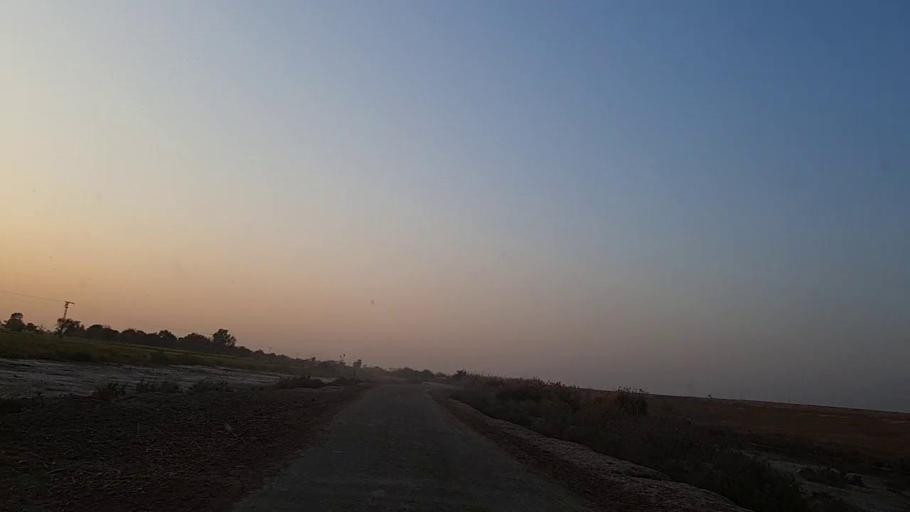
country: PK
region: Sindh
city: Bhit Shah
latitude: 25.9223
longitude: 68.4909
